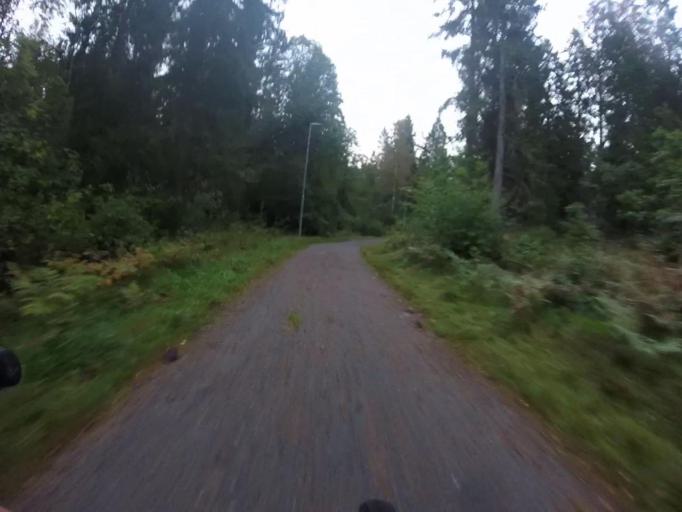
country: SE
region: Vaestra Goetaland
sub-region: Trollhattan
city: Trollhattan
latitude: 58.2918
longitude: 12.2666
